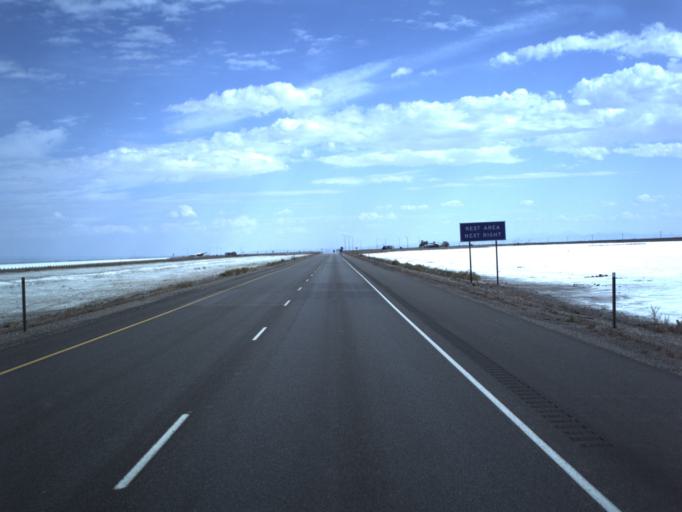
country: US
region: Utah
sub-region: Tooele County
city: Wendover
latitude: 40.7388
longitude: -113.8698
